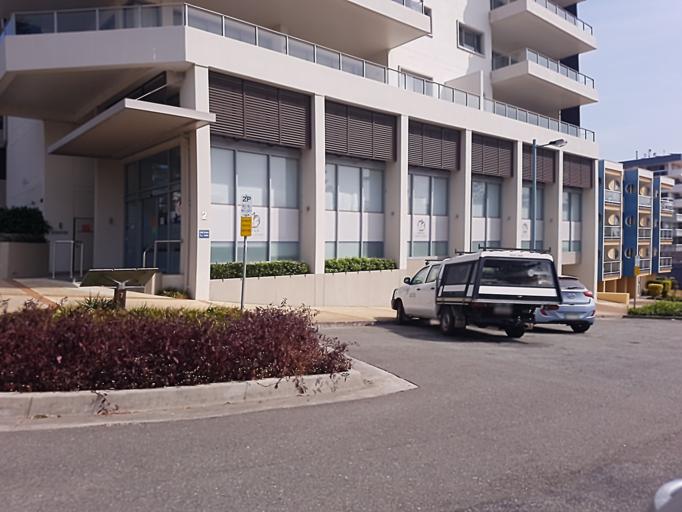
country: AU
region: New South Wales
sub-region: Port Macquarie-Hastings
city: Port Macquarie
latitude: -31.4289
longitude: 152.9131
